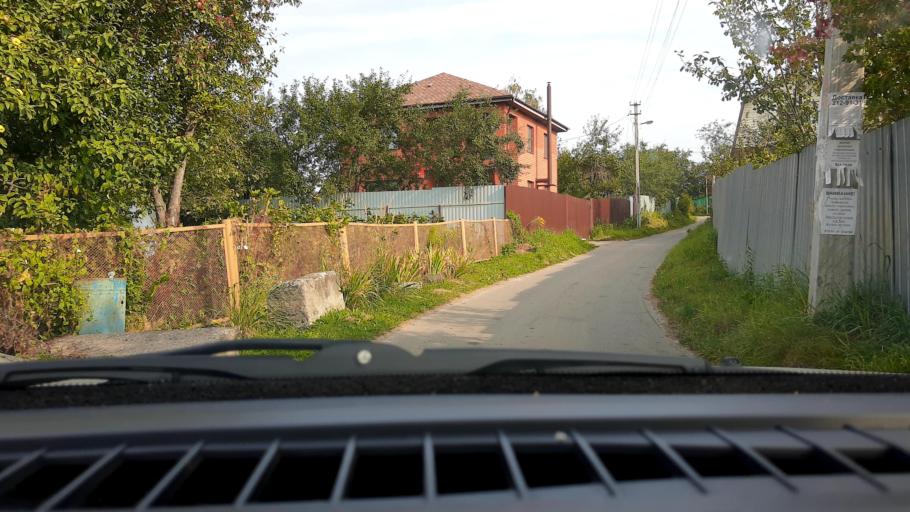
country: RU
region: Nizjnij Novgorod
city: Afonino
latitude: 56.1921
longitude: 44.0660
